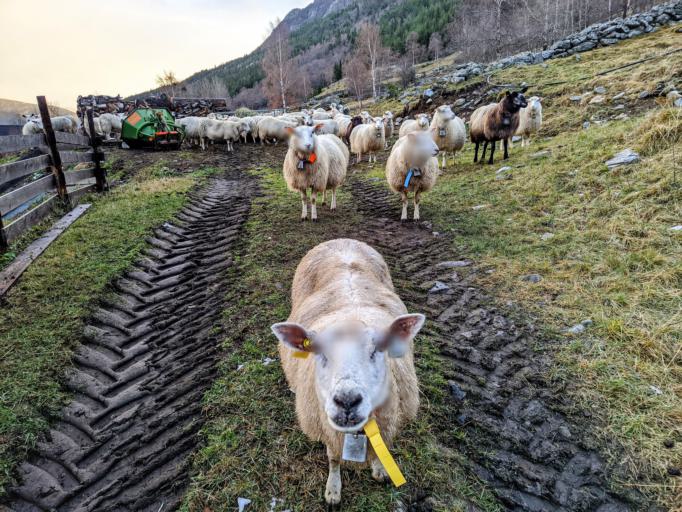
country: NO
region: Oppland
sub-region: Lom
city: Fossbergom
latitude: 61.8193
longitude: 8.5315
